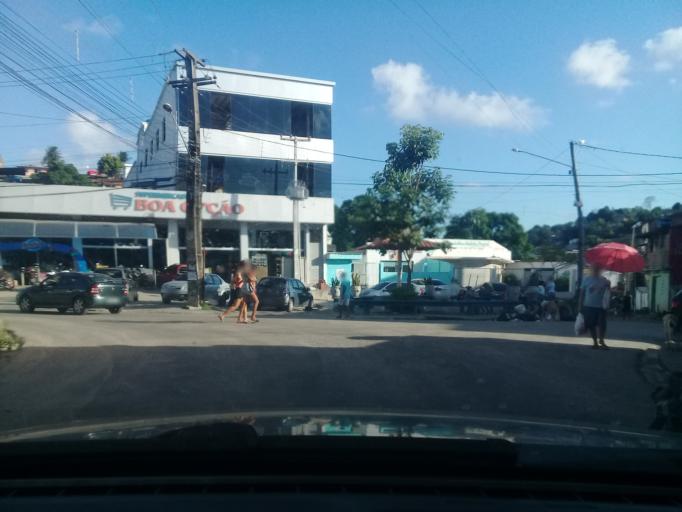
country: BR
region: Pernambuco
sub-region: Jaboatao Dos Guararapes
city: Jaboatao dos Guararapes
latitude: -8.1027
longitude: -34.9667
